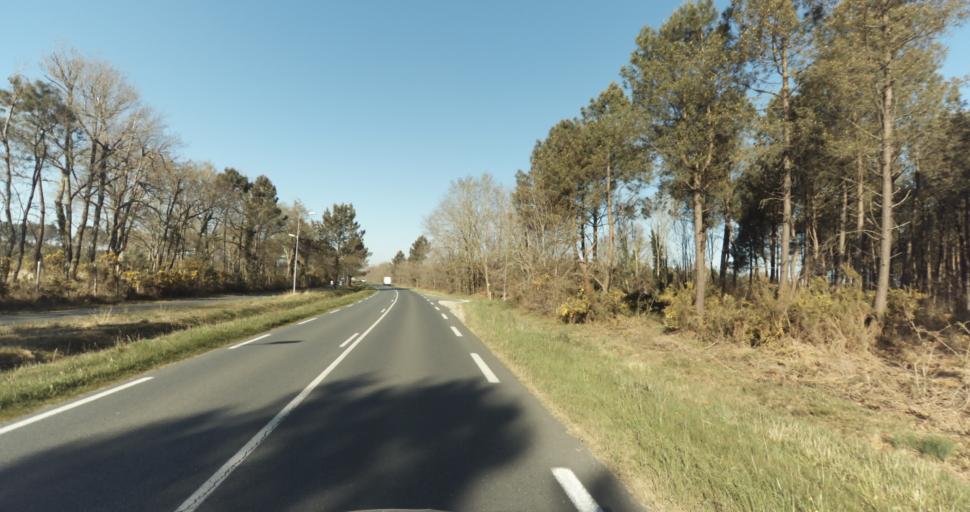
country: FR
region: Aquitaine
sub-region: Departement de la Gironde
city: Martignas-sur-Jalle
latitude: 44.8047
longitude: -0.8176
